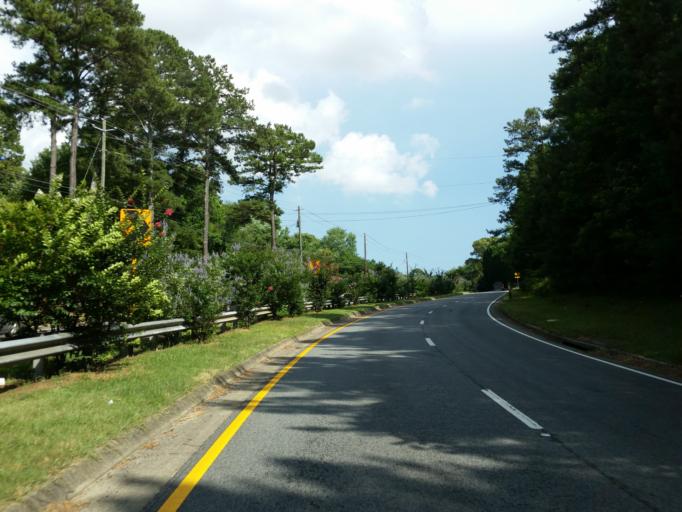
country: US
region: Georgia
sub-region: Cobb County
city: Marietta
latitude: 34.0198
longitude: -84.5123
